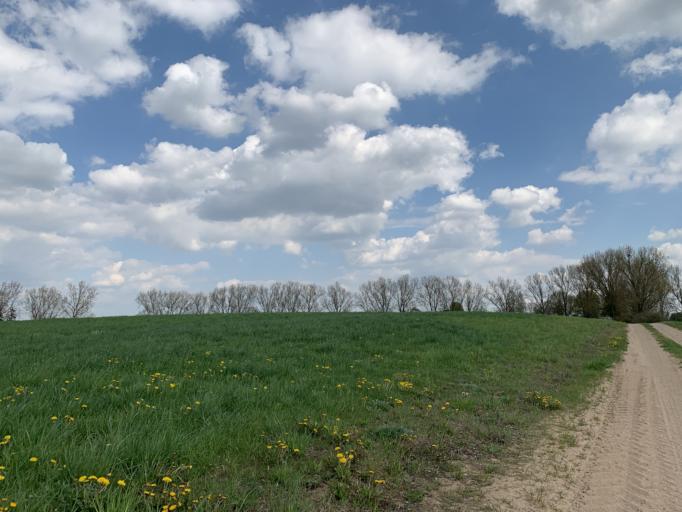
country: BY
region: Minsk
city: Nyasvizh
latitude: 53.2449
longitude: 26.6923
